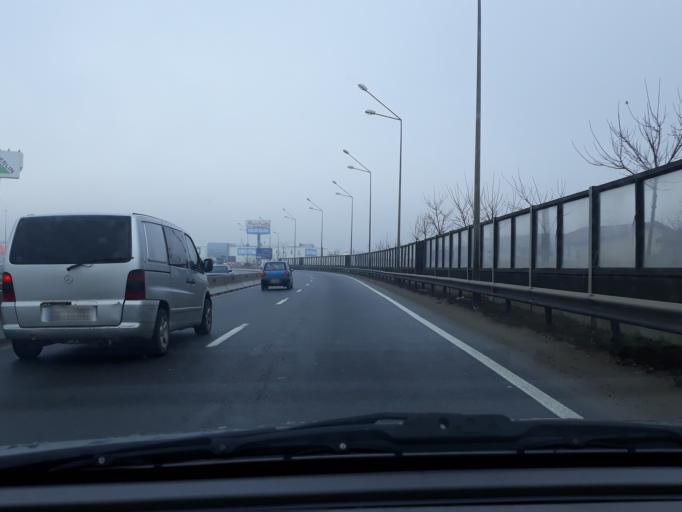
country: RO
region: Bihor
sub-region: Comuna Biharea
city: Oradea
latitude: 47.0429
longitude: 21.9116
